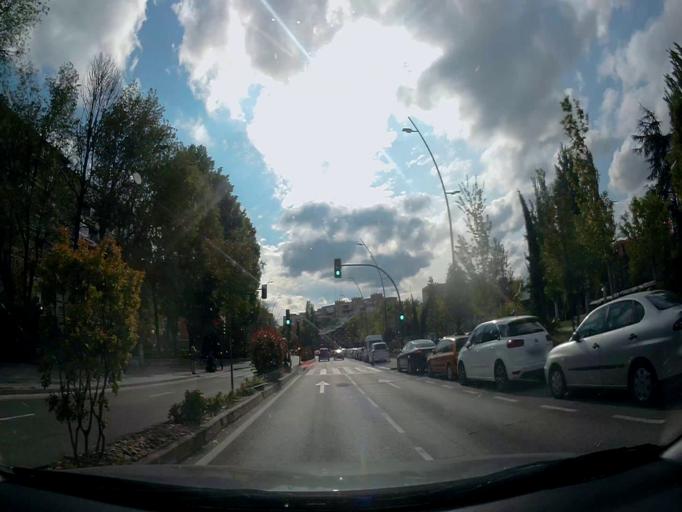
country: ES
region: Madrid
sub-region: Provincia de Madrid
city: Mostoles
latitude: 40.3263
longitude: -3.8671
